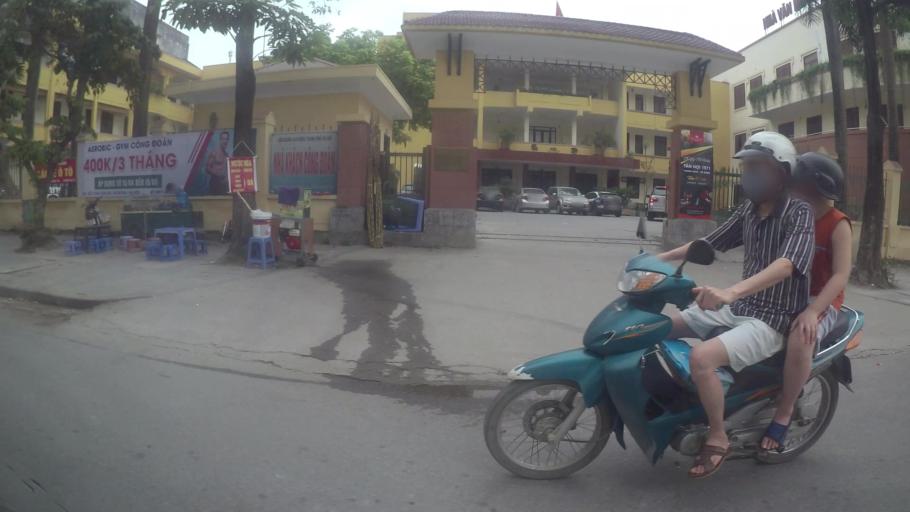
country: VN
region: Ha Noi
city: Ha Dong
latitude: 20.9740
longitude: 105.7781
